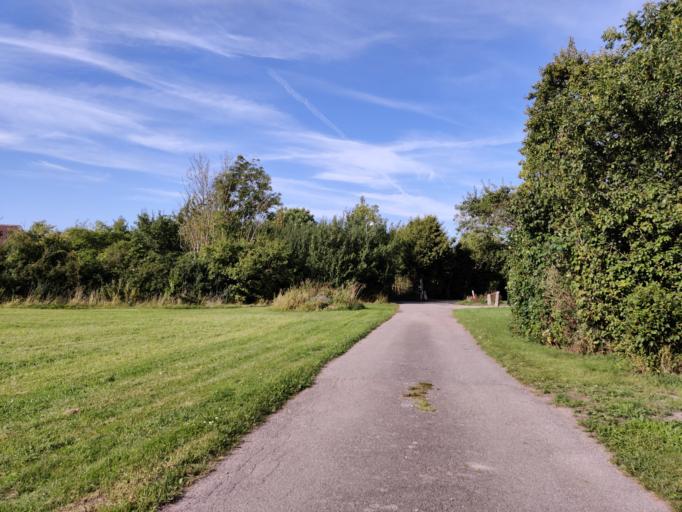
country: DK
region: Zealand
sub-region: Guldborgsund Kommune
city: Nykobing Falster
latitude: 54.6543
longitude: 11.8946
